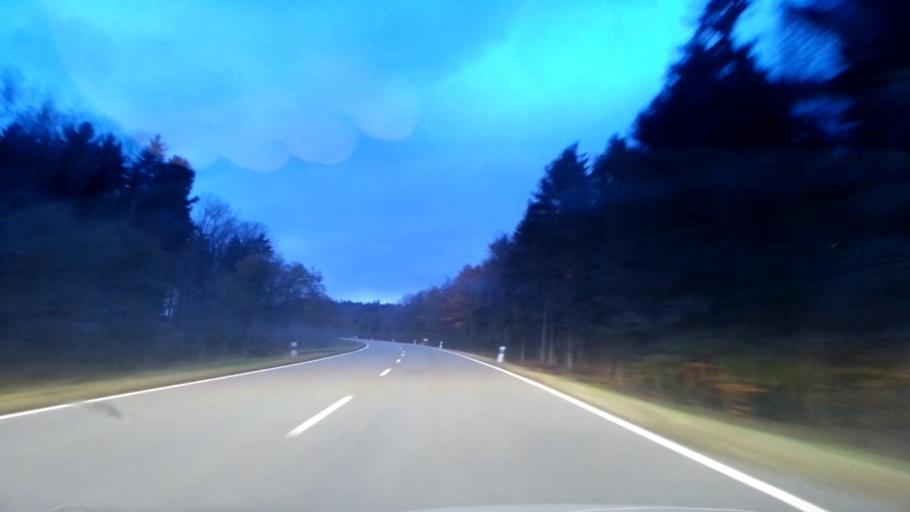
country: DE
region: Bavaria
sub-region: Upper Palatinate
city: Fuchsmuhl
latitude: 49.9357
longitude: 12.1291
